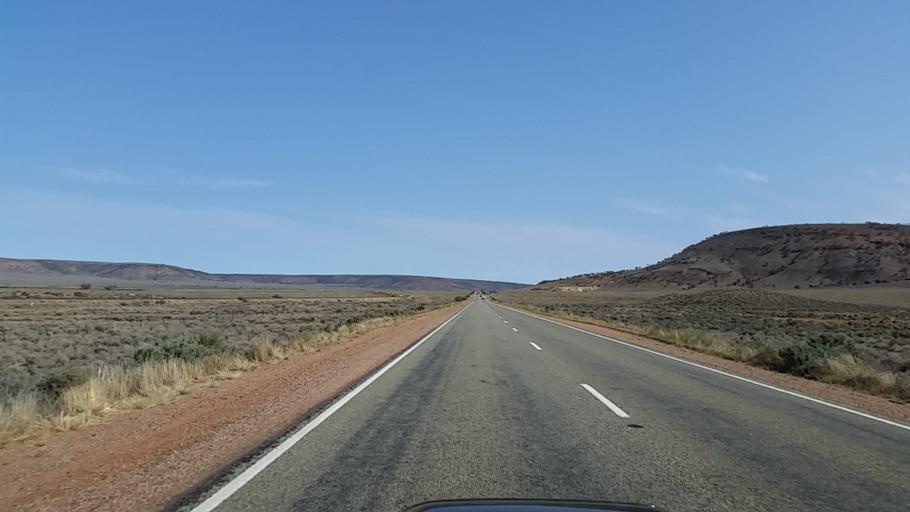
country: AU
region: South Australia
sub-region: Port Augusta
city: Port Augusta West
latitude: -32.5592
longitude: 137.6297
